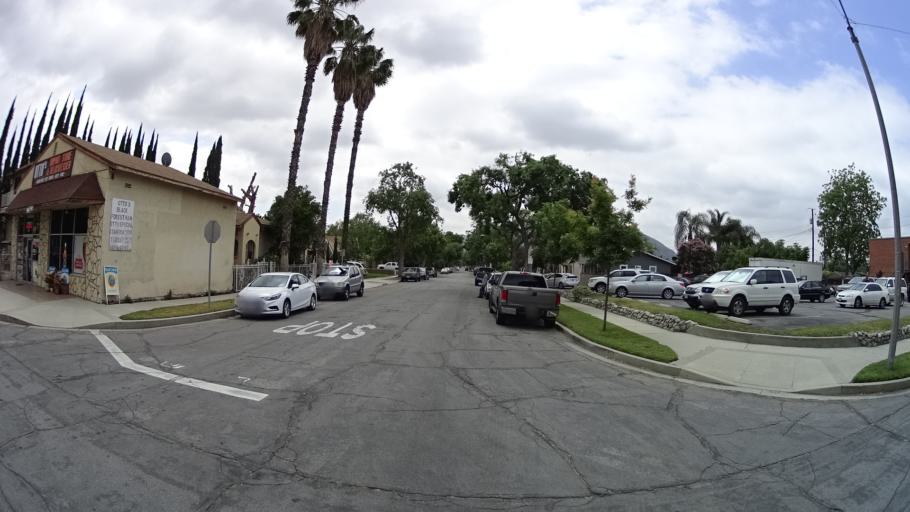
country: US
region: California
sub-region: Los Angeles County
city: Burbank
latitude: 34.1688
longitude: -118.3321
